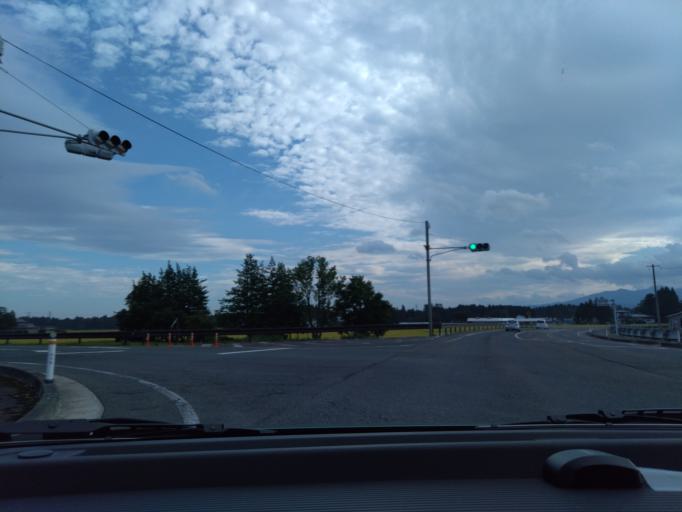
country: JP
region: Iwate
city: Hanamaki
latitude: 39.3377
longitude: 141.0486
